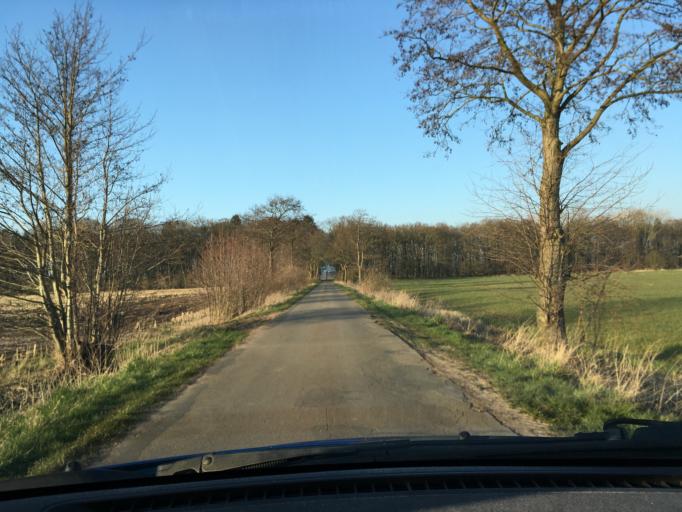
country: DE
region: Lower Saxony
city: Hittbergen
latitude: 53.3175
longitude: 10.6247
